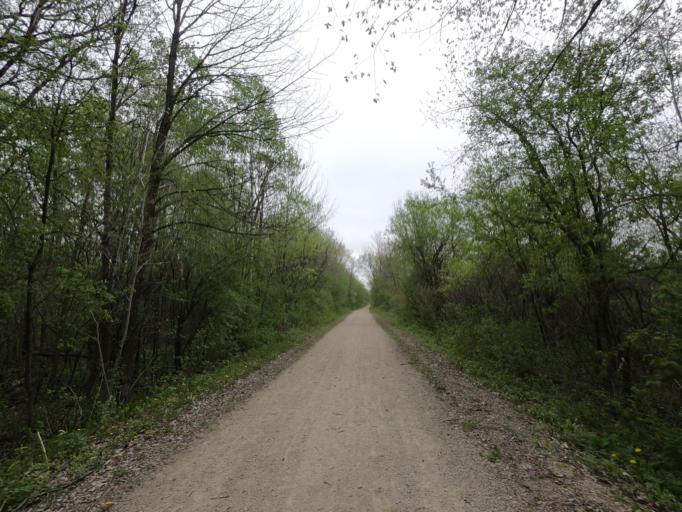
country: US
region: Wisconsin
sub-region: Jefferson County
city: Johnson Creek
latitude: 43.0349
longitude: -88.7564
